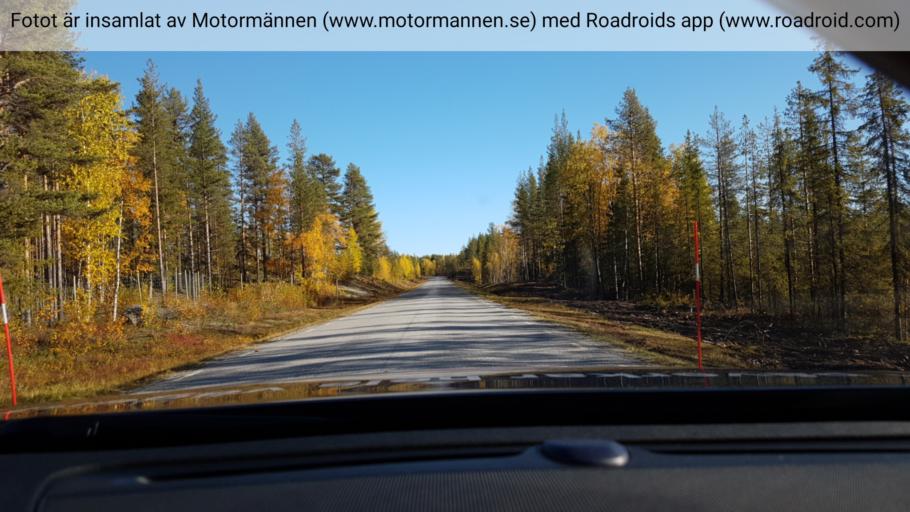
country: SE
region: Norrbotten
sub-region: Gallivare Kommun
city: Gaellivare
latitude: 66.4654
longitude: 20.8198
